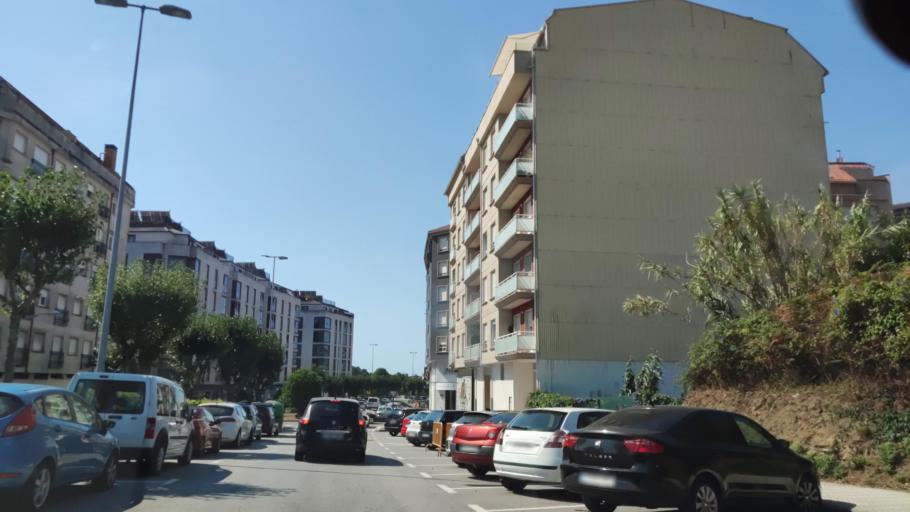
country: ES
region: Galicia
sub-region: Provincia da Coruna
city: Boiro
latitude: 42.6487
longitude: -8.8789
